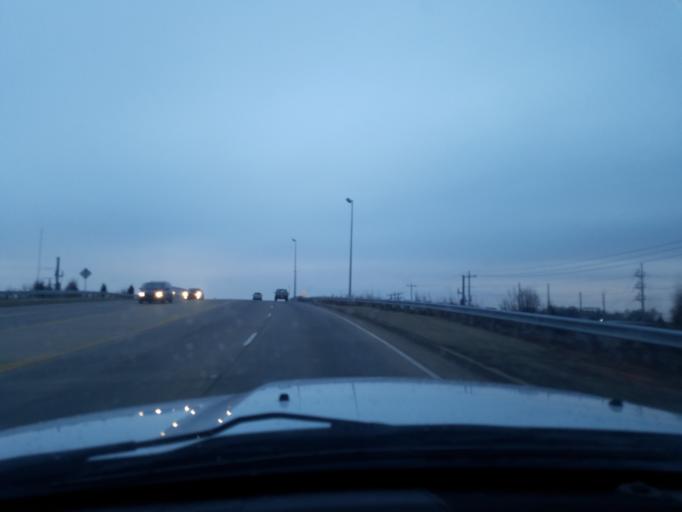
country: US
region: Kentucky
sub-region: Warren County
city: Bowling Green
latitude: 36.9674
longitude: -86.4792
